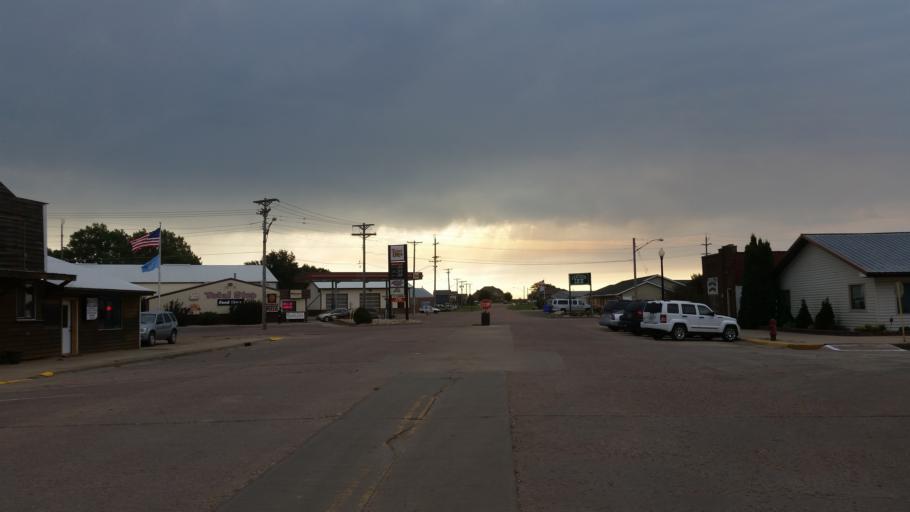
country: US
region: South Dakota
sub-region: McCook County
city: Salem
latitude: 43.5977
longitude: -97.2916
